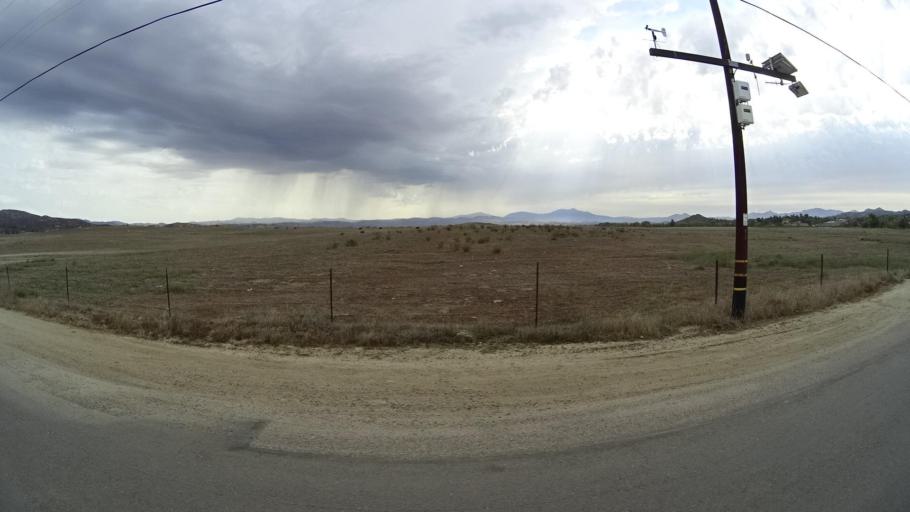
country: US
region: California
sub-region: San Diego County
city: San Pasqual
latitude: 33.0352
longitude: -116.9362
